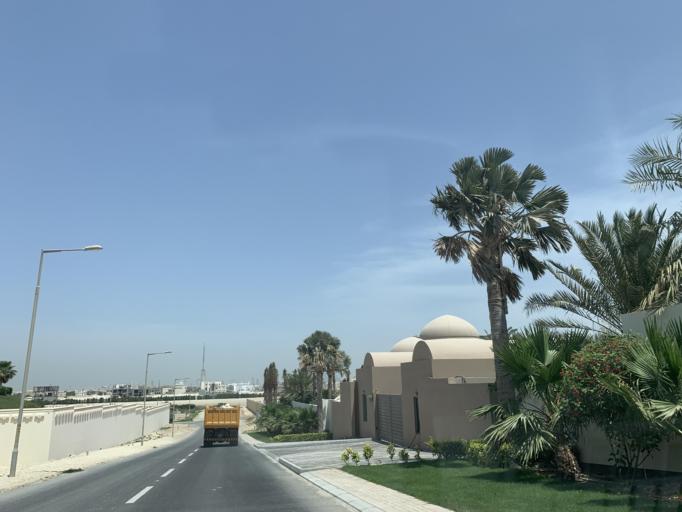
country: BH
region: Northern
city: Ar Rifa'
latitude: 26.1465
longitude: 50.5545
